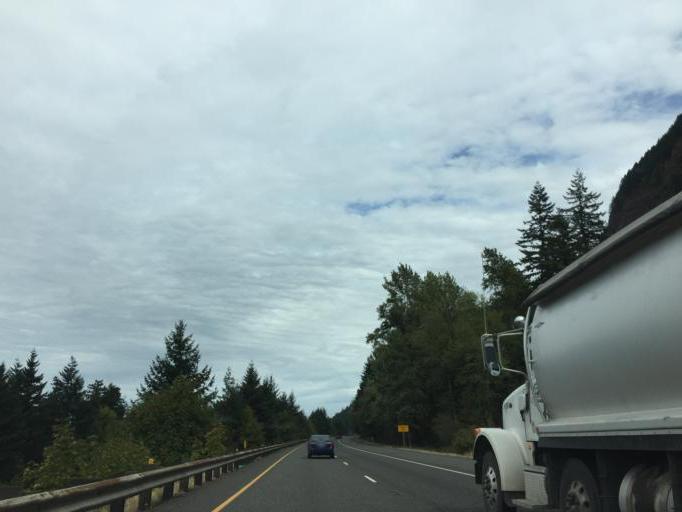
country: US
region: Oregon
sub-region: Hood River County
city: Cascade Locks
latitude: 45.6176
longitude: -121.9917
